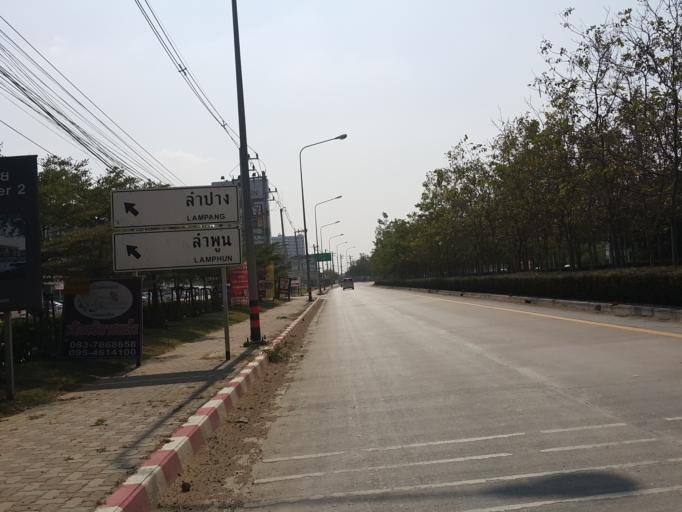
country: TH
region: Chiang Mai
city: Saraphi
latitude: 18.7567
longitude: 99.0369
